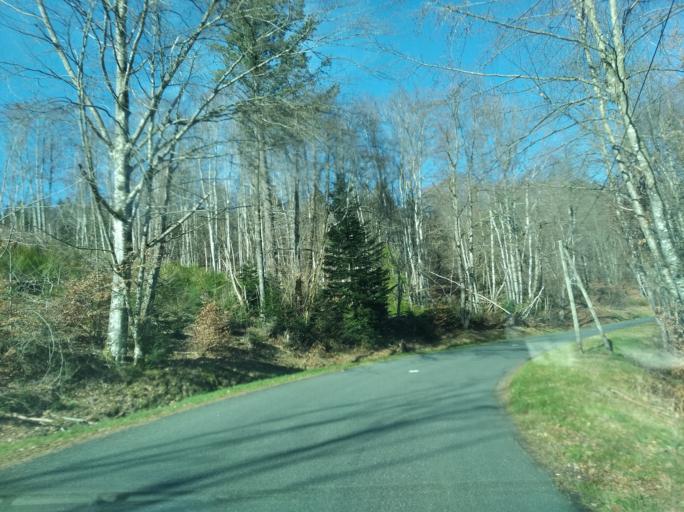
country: FR
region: Auvergne
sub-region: Departement de l'Allier
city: Le Mayet-de-Montagne
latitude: 46.1009
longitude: 3.7721
